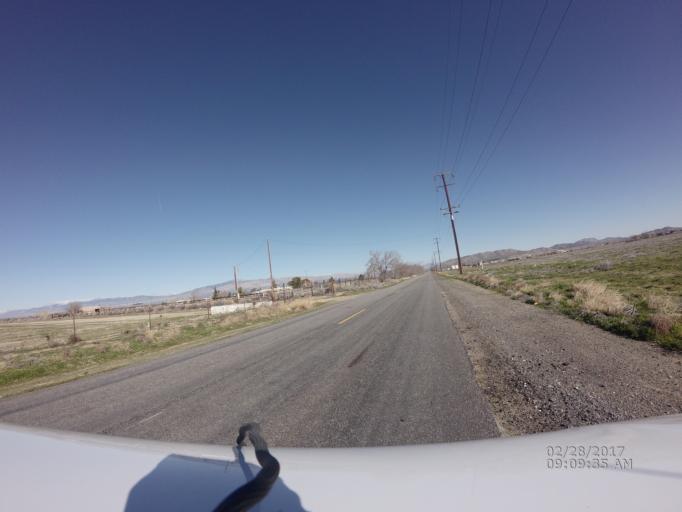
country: US
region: California
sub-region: Kern County
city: Rosamond
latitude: 34.8219
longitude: -118.2905
